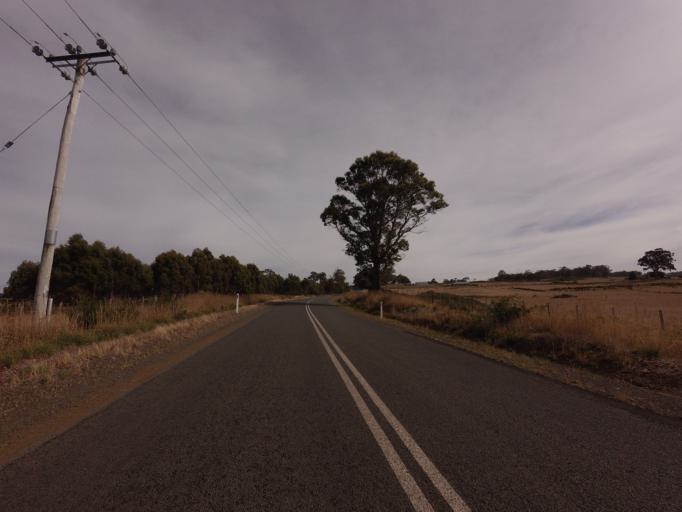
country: AU
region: Tasmania
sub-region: Sorell
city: Sorell
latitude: -42.4134
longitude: 147.4574
